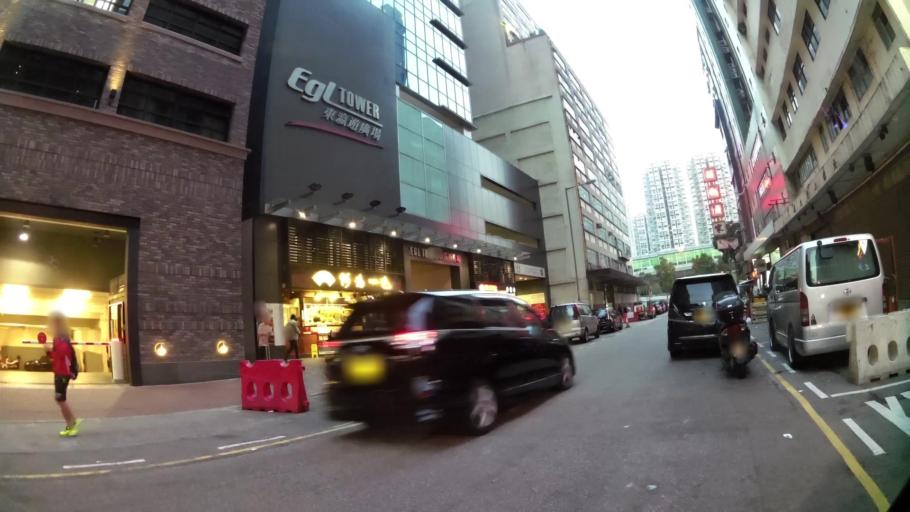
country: HK
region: Kowloon City
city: Kowloon
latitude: 22.3082
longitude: 114.2246
